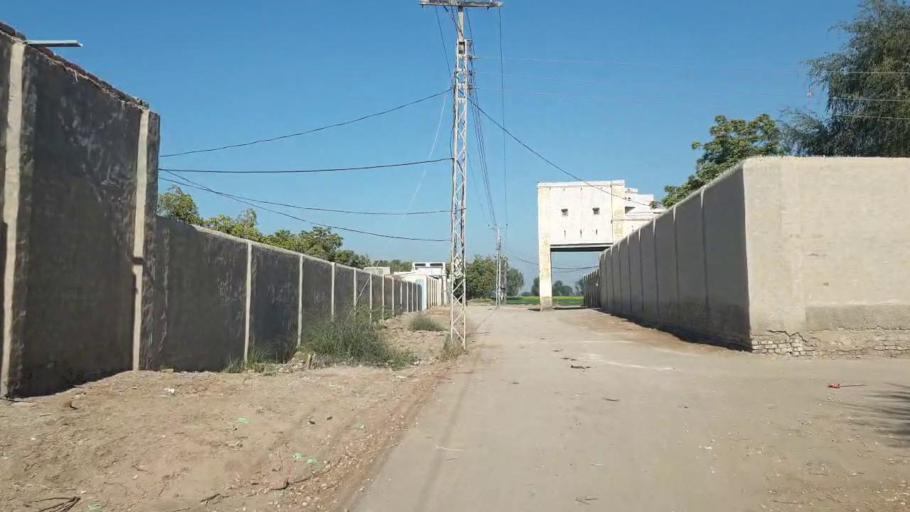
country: PK
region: Sindh
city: Shahpur Chakar
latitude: 26.1046
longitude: 68.6341
